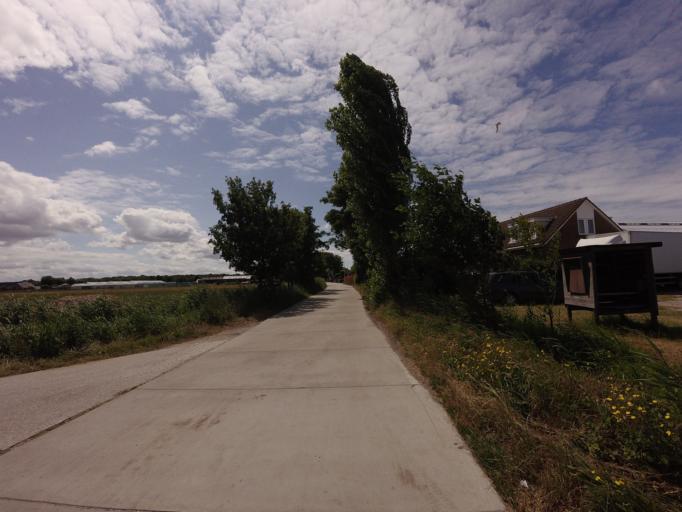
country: NL
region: South Holland
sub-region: Gemeente Teylingen
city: Sassenheim
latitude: 52.2127
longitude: 4.5151
